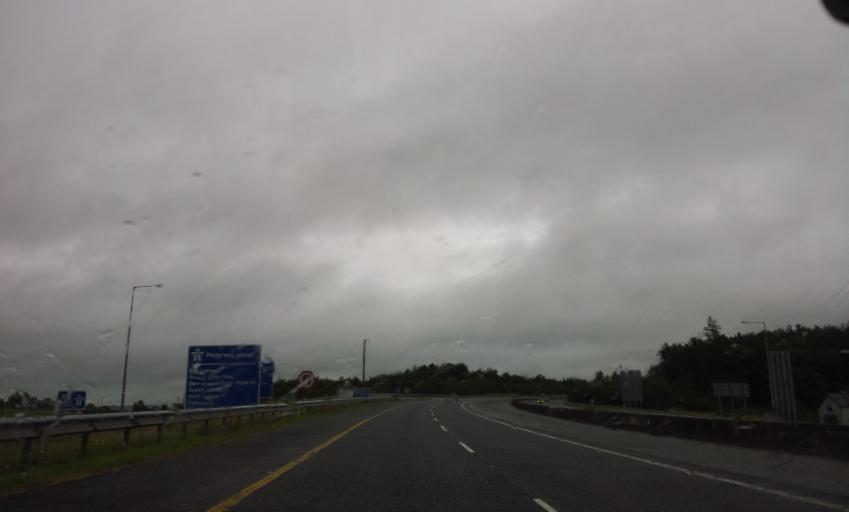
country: IE
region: Munster
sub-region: County Cork
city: Fermoy
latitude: 52.1159
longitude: -8.2726
